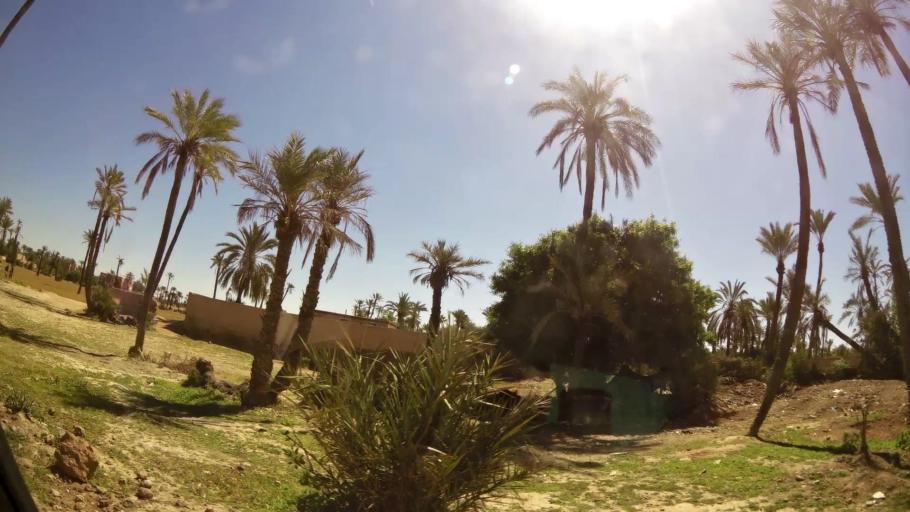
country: MA
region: Marrakech-Tensift-Al Haouz
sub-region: Marrakech
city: Marrakesh
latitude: 31.6771
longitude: -7.9803
